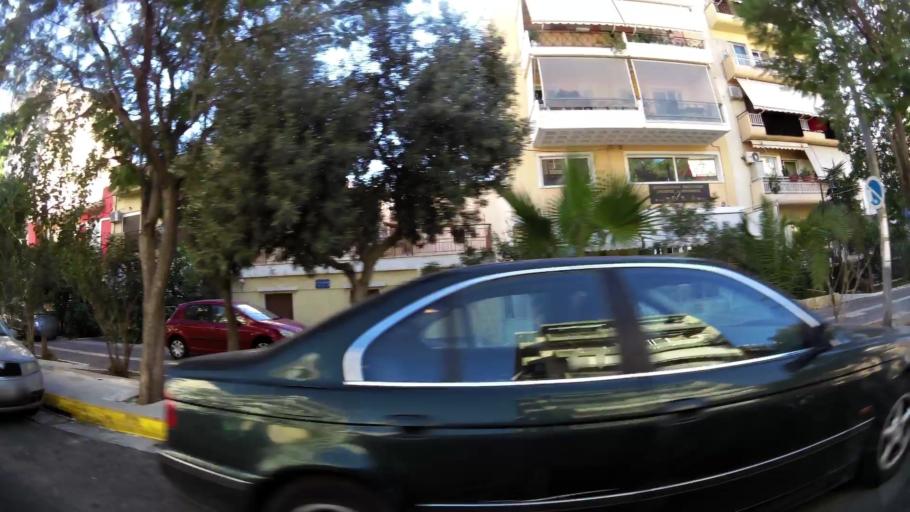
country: GR
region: Attica
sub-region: Nomos Piraios
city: Perama
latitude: 37.9642
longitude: 23.5643
